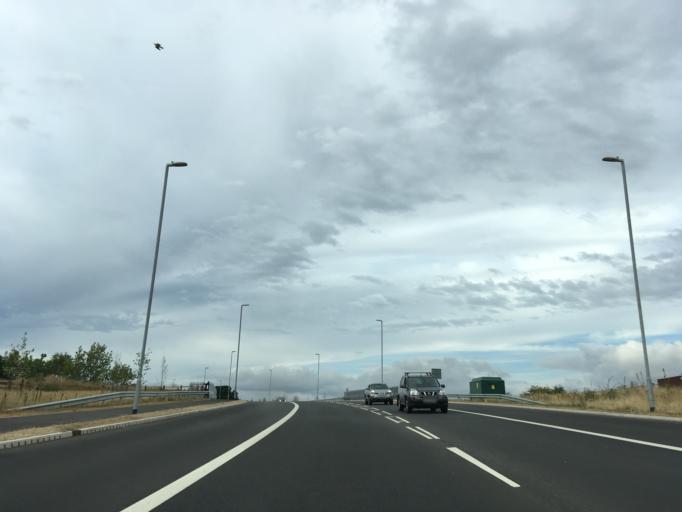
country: GB
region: England
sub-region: South Gloucestershire
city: Stoke Gifford
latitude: 51.5134
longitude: -2.5286
